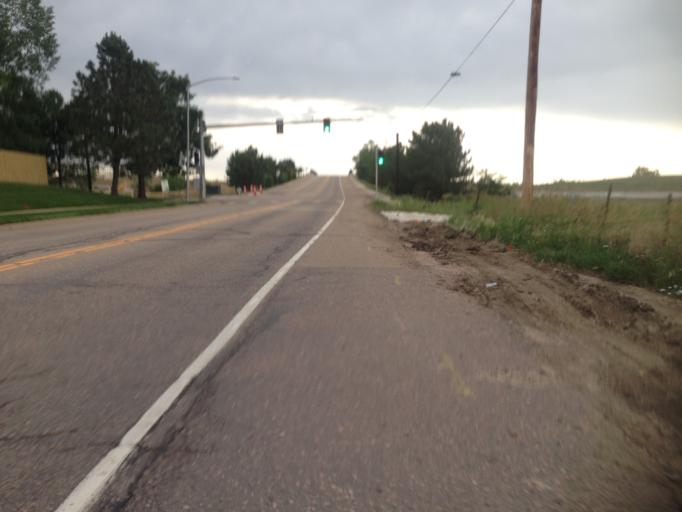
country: US
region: Colorado
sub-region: Boulder County
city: Superior
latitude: 39.9429
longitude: -105.1470
